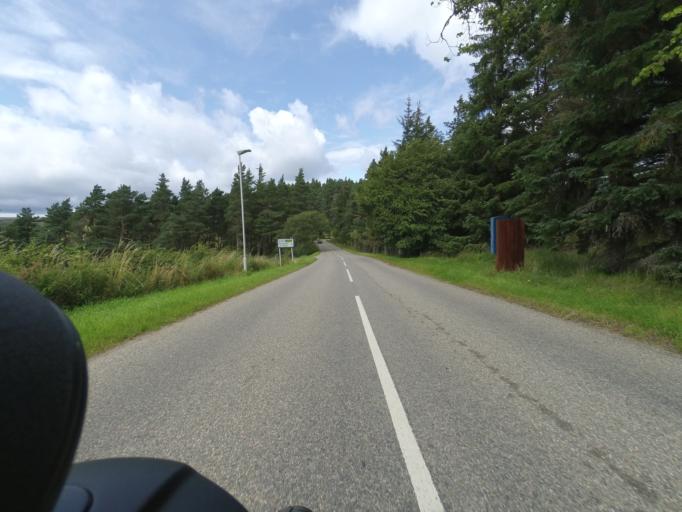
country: GB
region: Scotland
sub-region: Highland
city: Grantown on Spey
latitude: 57.2567
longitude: -3.3859
